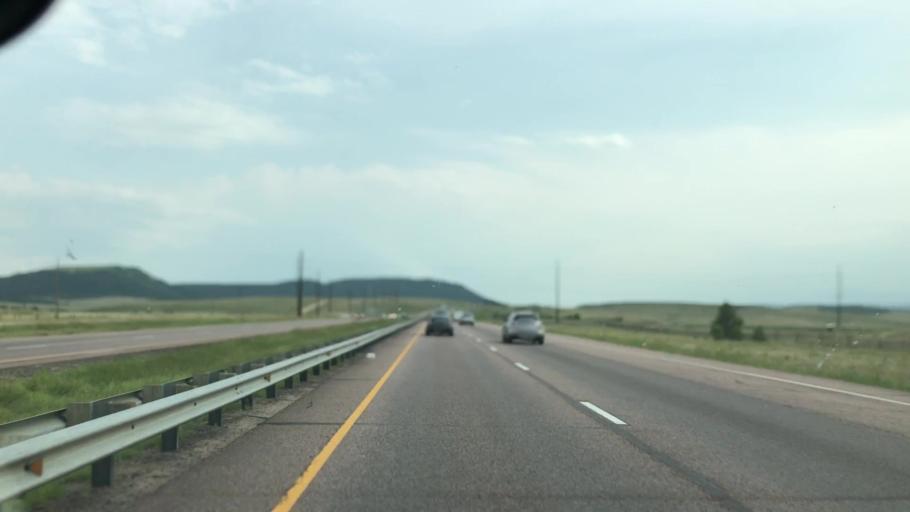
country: US
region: Colorado
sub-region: El Paso County
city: Woodmoor
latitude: 39.1833
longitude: -104.8503
